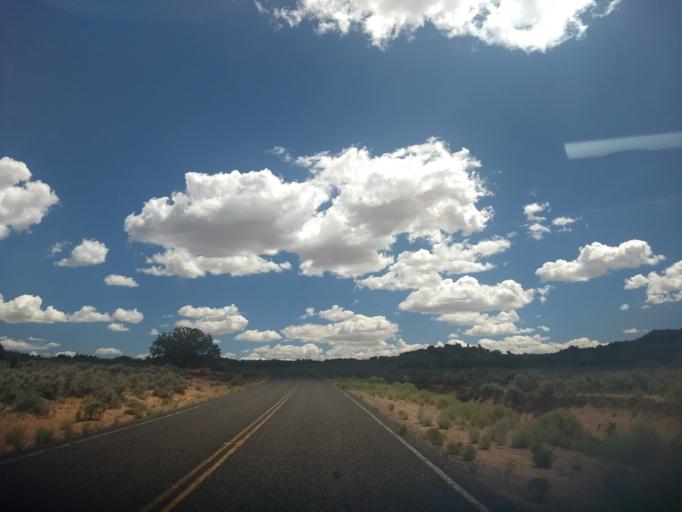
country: US
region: Utah
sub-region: Kane County
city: Kanab
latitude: 37.1348
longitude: -112.6762
